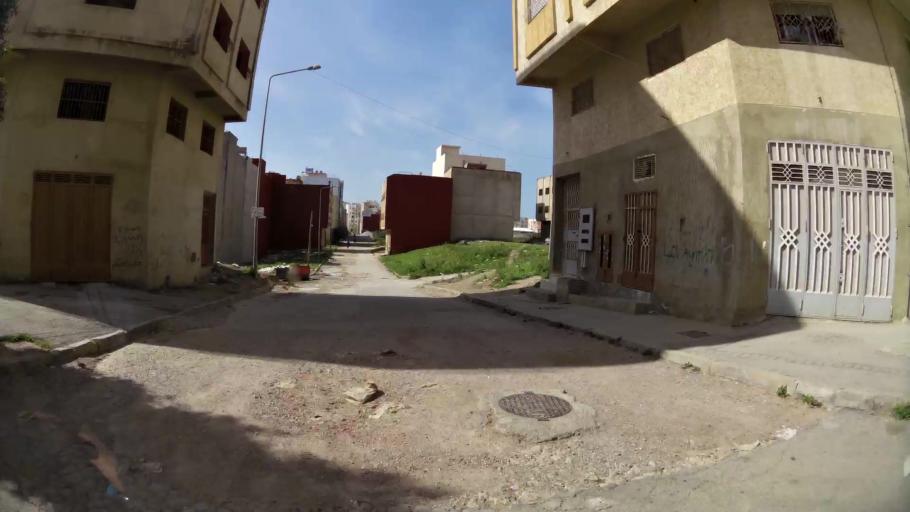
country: MA
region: Tanger-Tetouan
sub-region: Tanger-Assilah
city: Tangier
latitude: 35.7267
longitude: -5.8060
